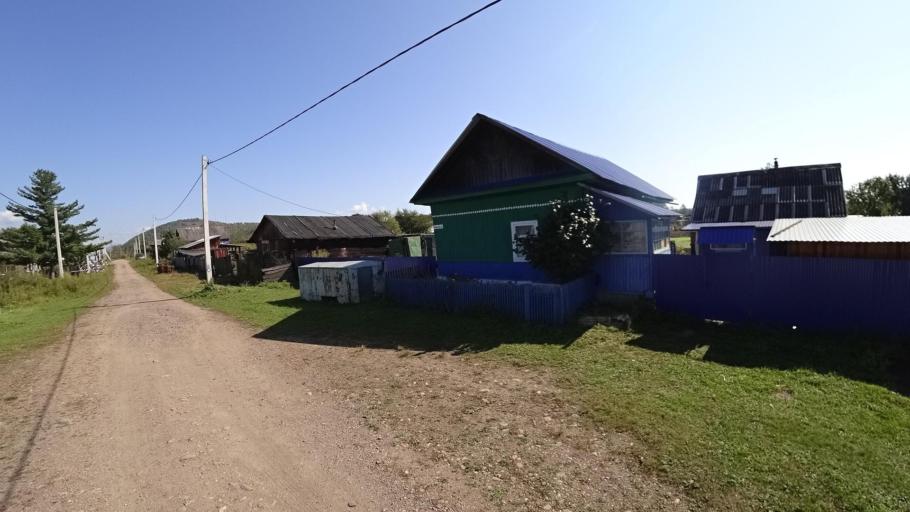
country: RU
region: Jewish Autonomous Oblast
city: Bira
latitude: 48.9978
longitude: 132.4498
